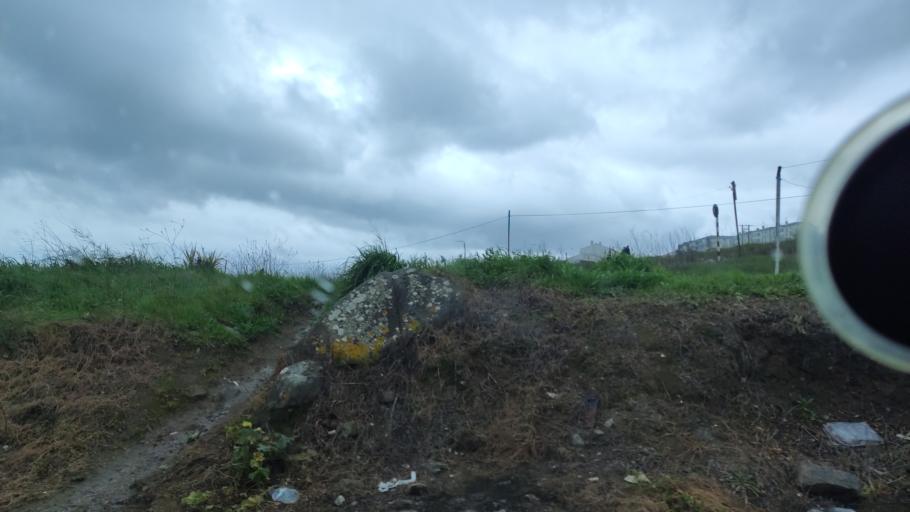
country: PT
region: Beja
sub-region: Beja
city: Beja
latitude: 38.0136
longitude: -7.8511
